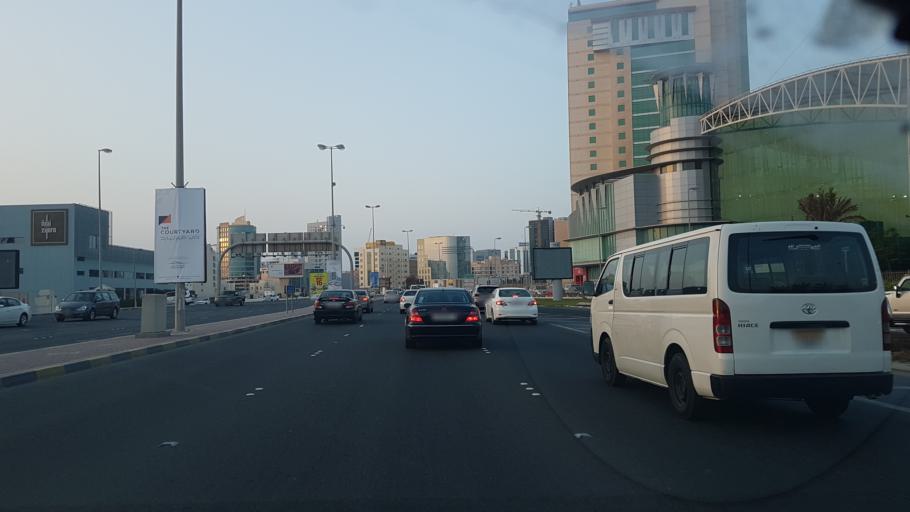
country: BH
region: Manama
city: Jidd Hafs
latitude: 26.2314
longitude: 50.5346
